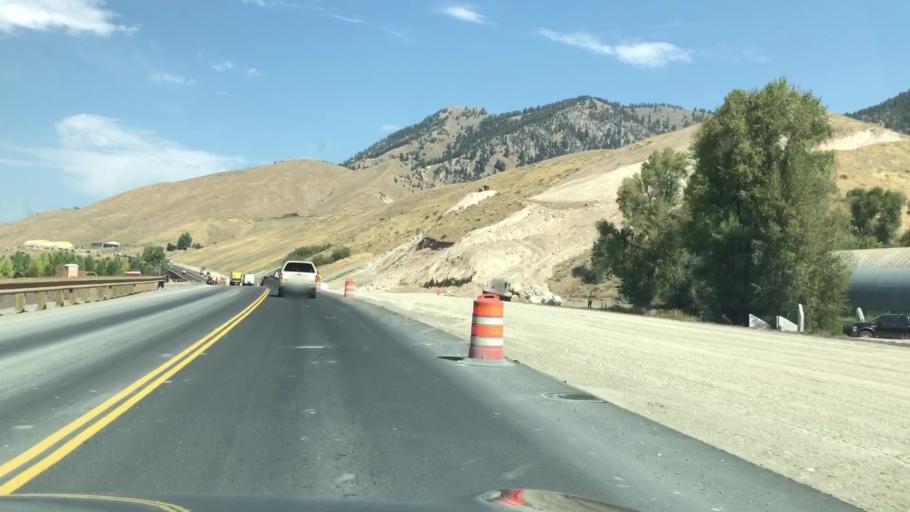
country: US
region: Wyoming
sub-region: Teton County
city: South Park
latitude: 43.3928
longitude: -110.7478
